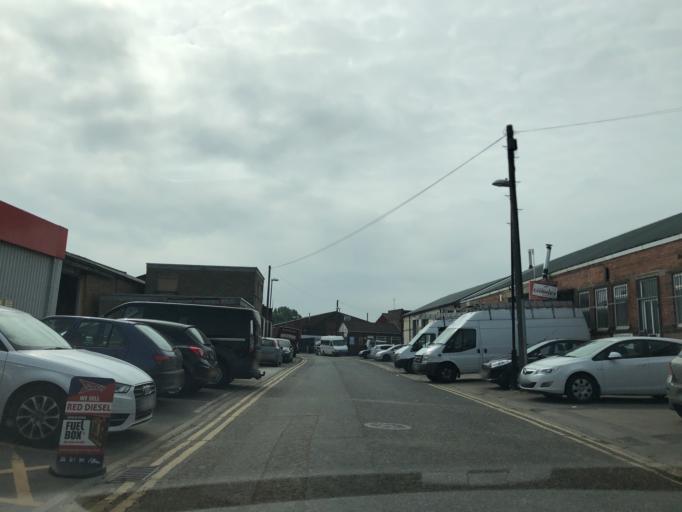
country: GB
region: England
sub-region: North Yorkshire
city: Knaresborough
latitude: 54.0005
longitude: -1.5016
